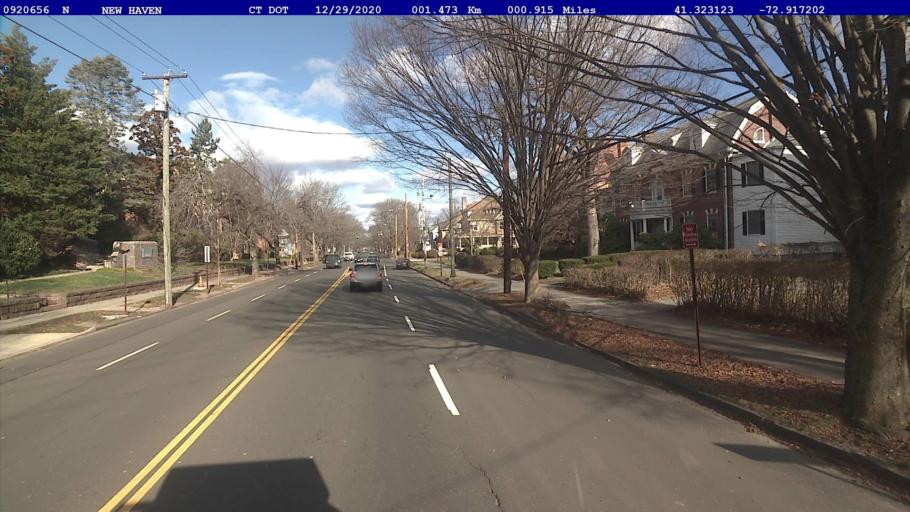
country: US
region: Connecticut
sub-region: New Haven County
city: New Haven
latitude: 41.3231
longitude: -72.9172
